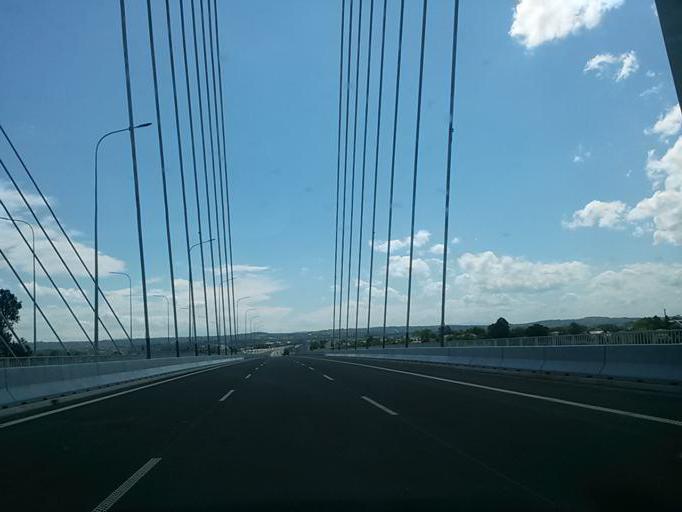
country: PL
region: Lesser Poland Voivodeship
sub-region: Powiat wielicki
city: Kokotow
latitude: 50.0504
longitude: 20.0722
